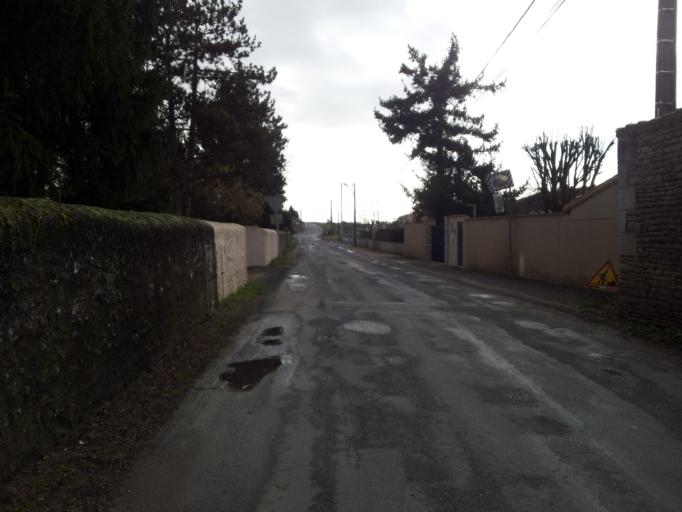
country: FR
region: Poitou-Charentes
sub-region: Departement de la Vienne
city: Avanton
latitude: 46.6582
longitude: 0.3354
